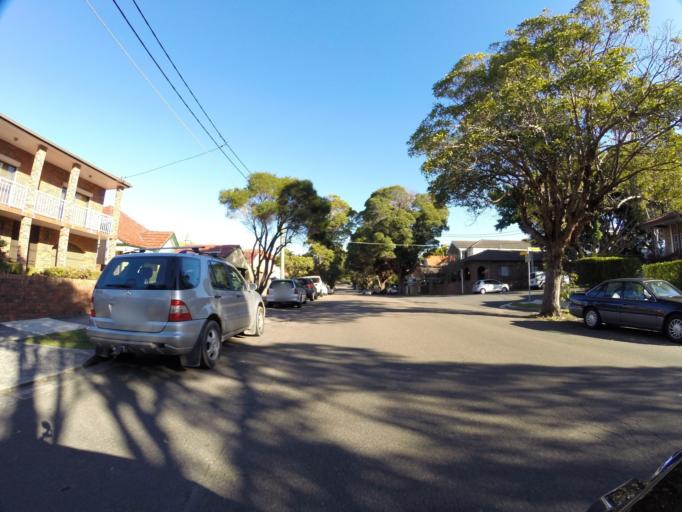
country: AU
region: New South Wales
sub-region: Waverley
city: Bondi
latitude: -33.8954
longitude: 151.2622
